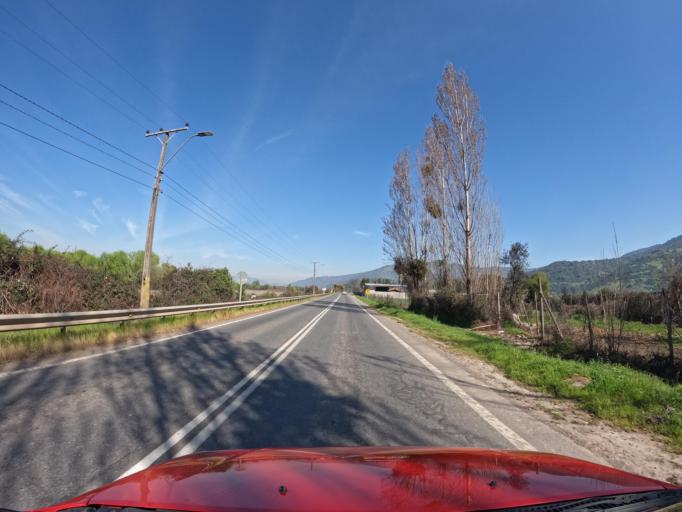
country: CL
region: Maule
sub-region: Provincia de Curico
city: Rauco
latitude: -34.9801
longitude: -71.4052
